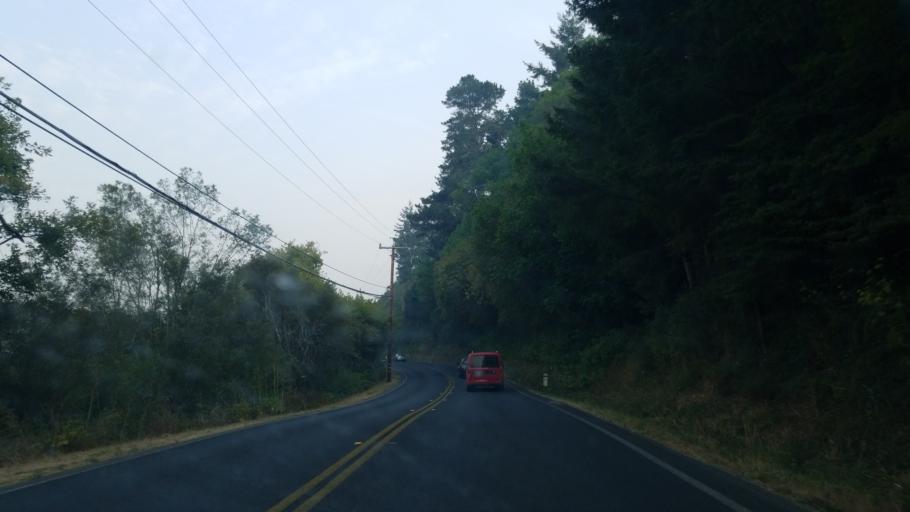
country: US
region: California
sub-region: Marin County
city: Inverness
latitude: 38.0669
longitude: -122.8227
